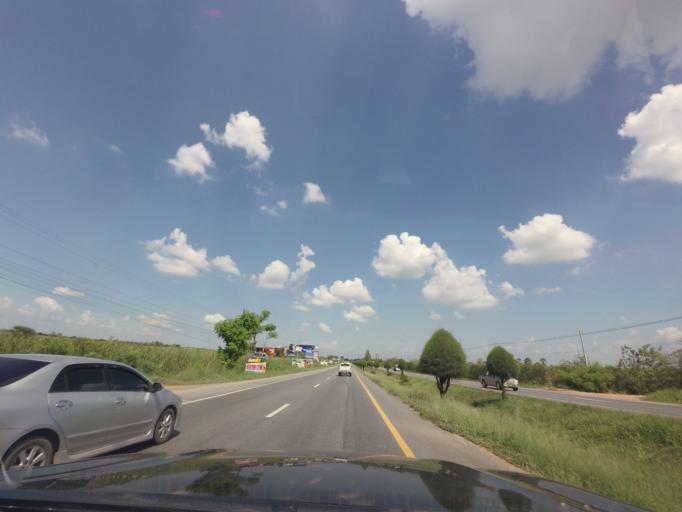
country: TH
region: Nakhon Ratchasima
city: Nakhon Ratchasima
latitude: 15.0540
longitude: 102.1394
